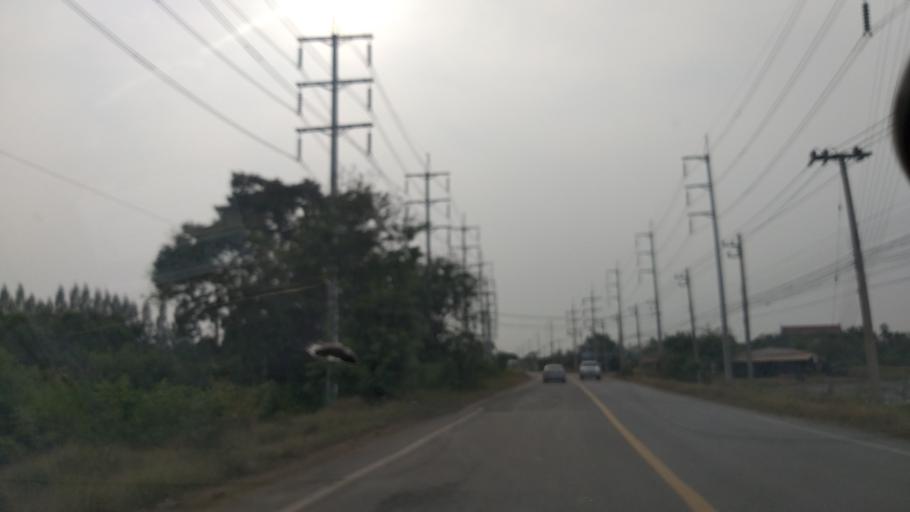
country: TH
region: Chachoengsao
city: Ban Pho
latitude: 13.6045
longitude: 101.1316
